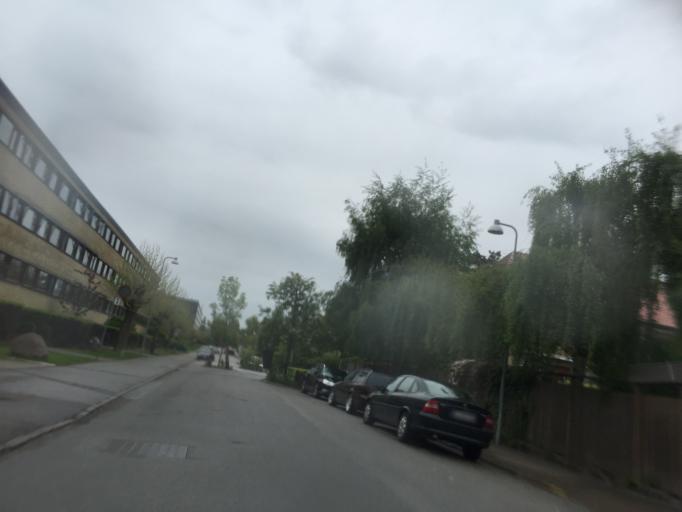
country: DK
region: Capital Region
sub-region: Frederiksberg Kommune
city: Frederiksberg
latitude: 55.6910
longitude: 12.5215
